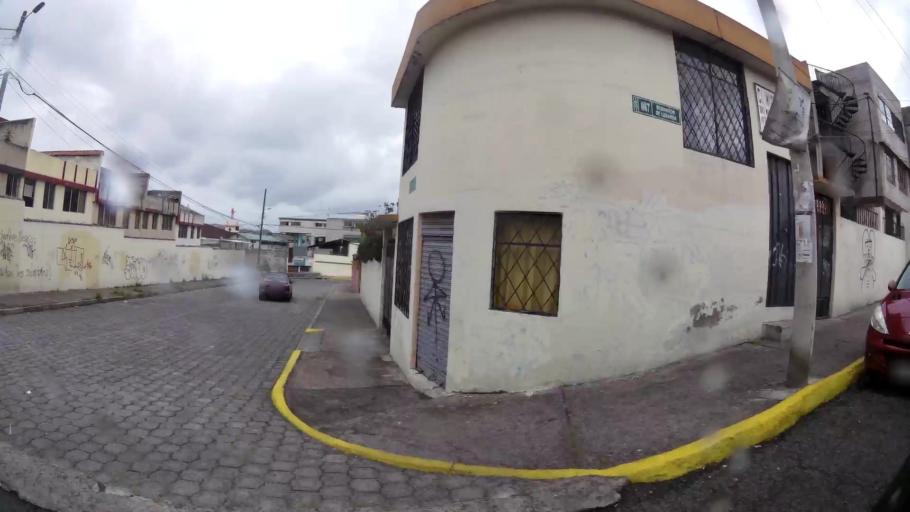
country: EC
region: Pichincha
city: Quito
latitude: -0.1153
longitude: -78.5005
